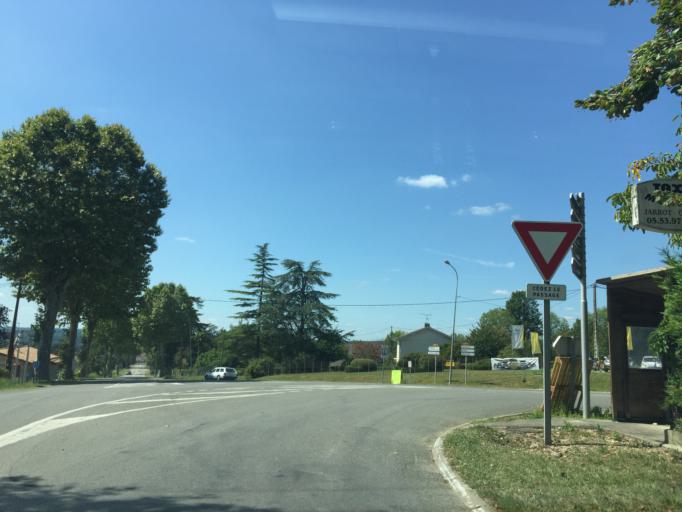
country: FR
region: Aquitaine
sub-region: Departement du Lot-et-Garonne
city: Mezin
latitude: 44.0543
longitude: 0.2695
